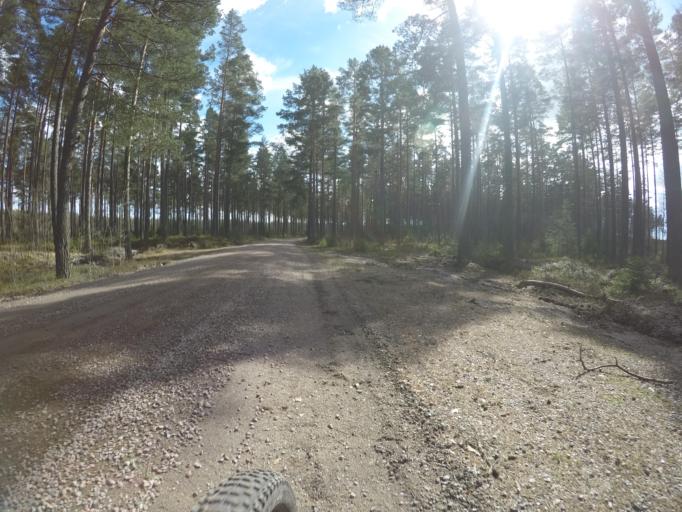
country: SE
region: Vaestmanland
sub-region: Kungsors Kommun
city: Kungsoer
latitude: 59.3712
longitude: 16.1004
